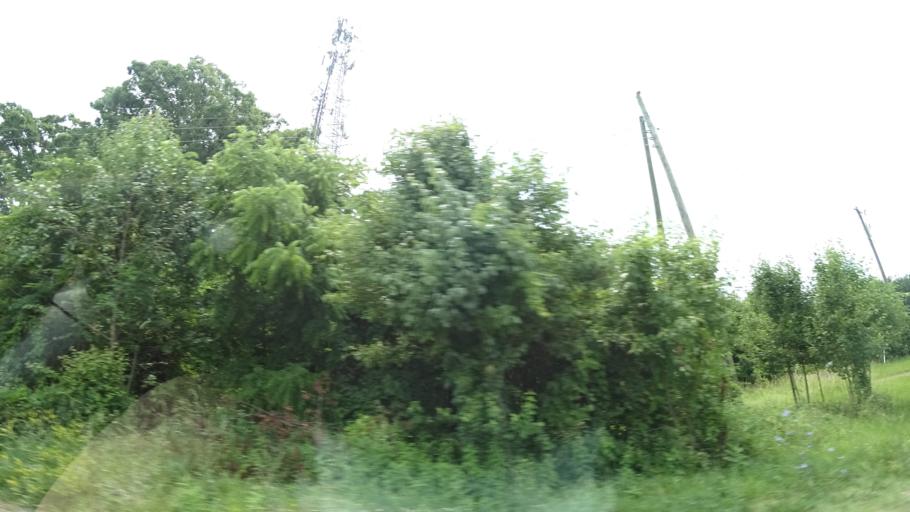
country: US
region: Virginia
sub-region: Fairfax County
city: Lorton
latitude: 38.6834
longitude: -77.2361
